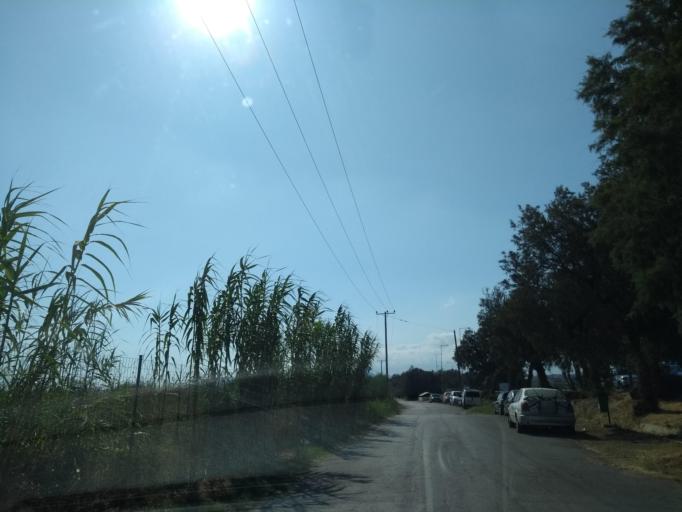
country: GR
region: Crete
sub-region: Nomos Chanias
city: Georgioupolis
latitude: 35.3547
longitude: 24.2806
